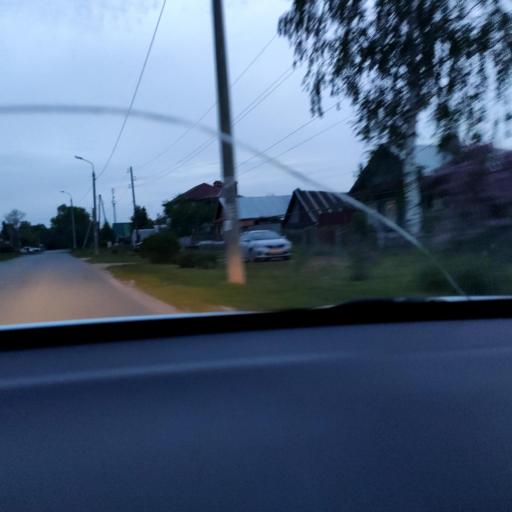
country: RU
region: Tatarstan
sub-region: Gorod Kazan'
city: Kazan
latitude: 55.7014
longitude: 49.0718
